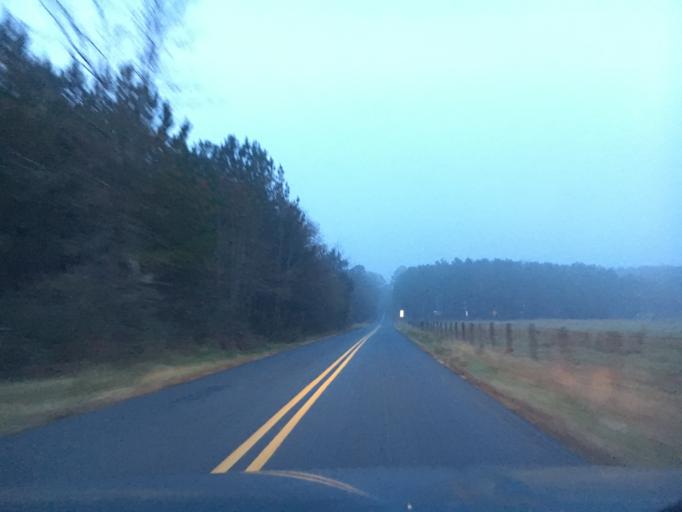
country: US
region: Virginia
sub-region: Halifax County
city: Mountain Road
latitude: 36.6823
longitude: -79.0311
